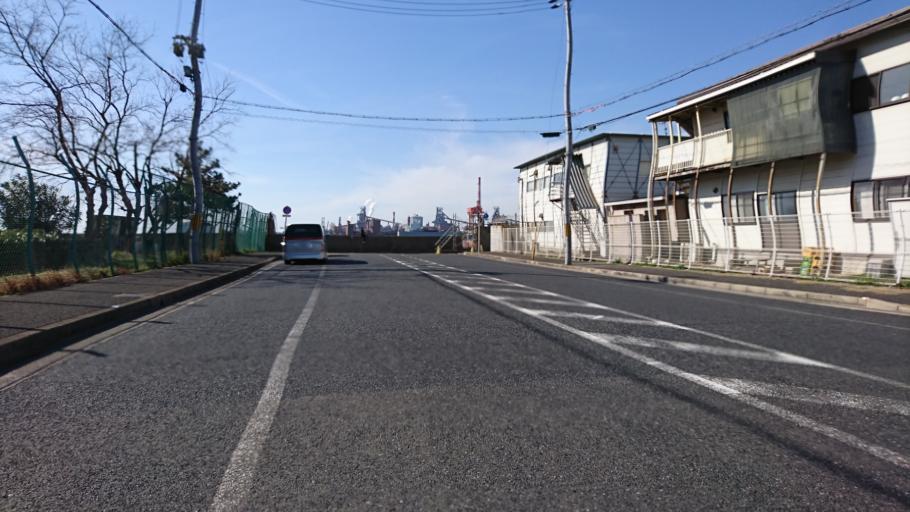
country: JP
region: Hyogo
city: Kakogawacho-honmachi
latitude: 34.7047
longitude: 134.8447
